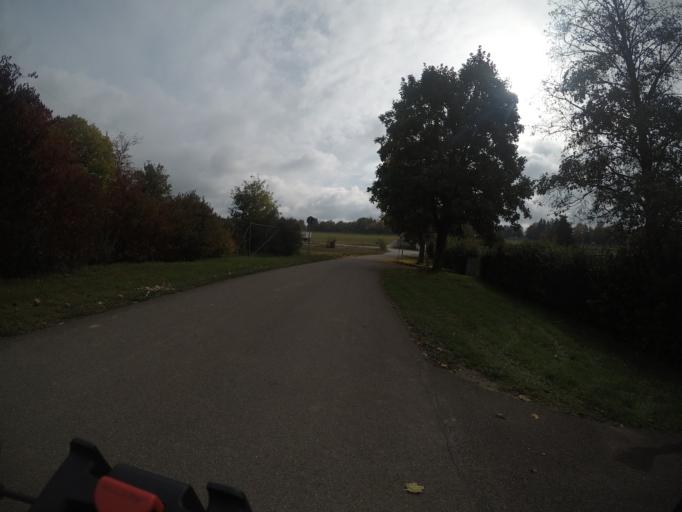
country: DE
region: Baden-Wuerttemberg
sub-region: Tuebingen Region
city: Dornstadt
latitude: 48.4553
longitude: 9.9493
